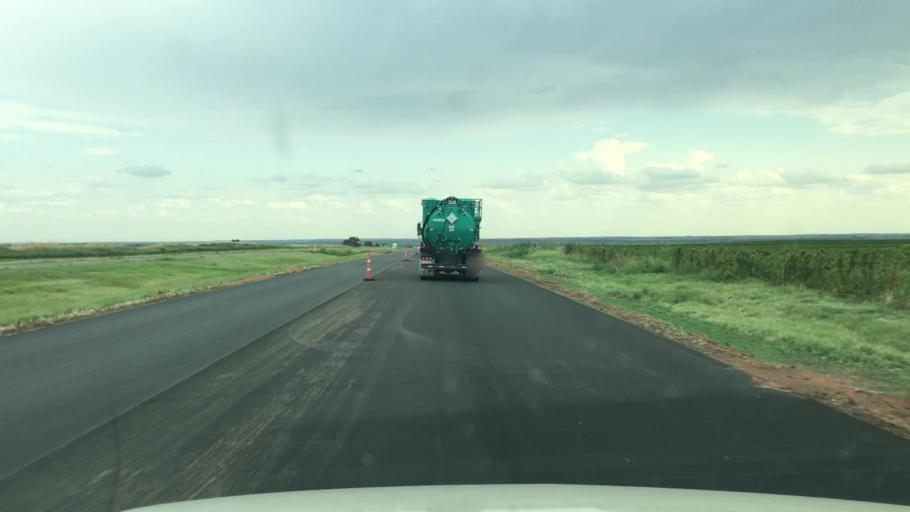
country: US
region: Texas
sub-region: Hall County
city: Memphis
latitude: 34.6153
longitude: -100.4704
